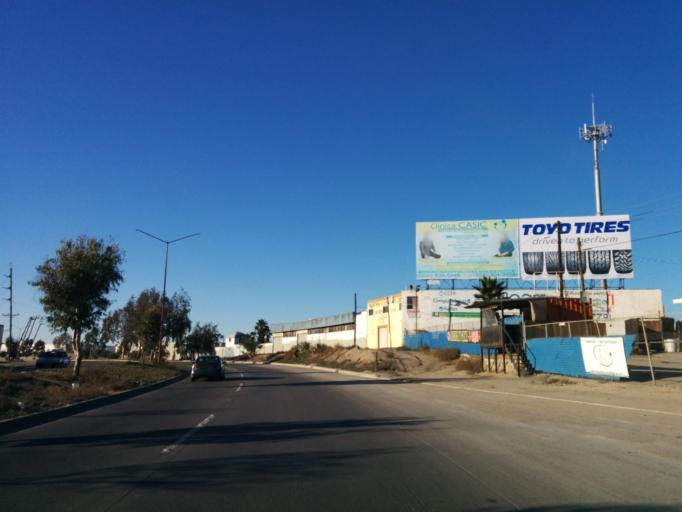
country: MX
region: Baja California
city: Tijuana
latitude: 32.5475
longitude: -116.9485
